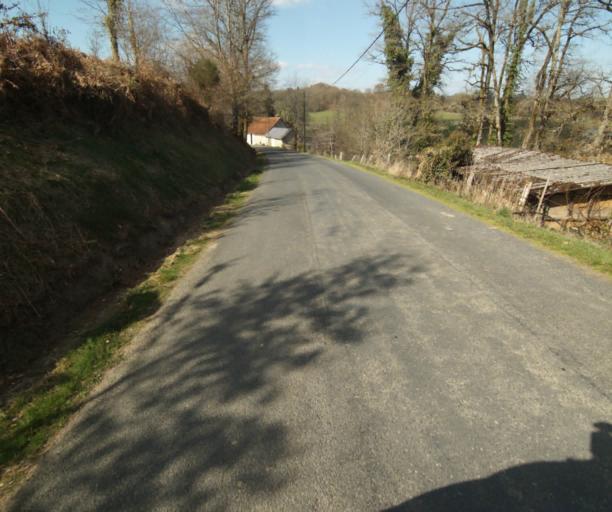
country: FR
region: Limousin
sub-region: Departement de la Correze
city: Saint-Mexant
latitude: 45.2917
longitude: 1.6171
